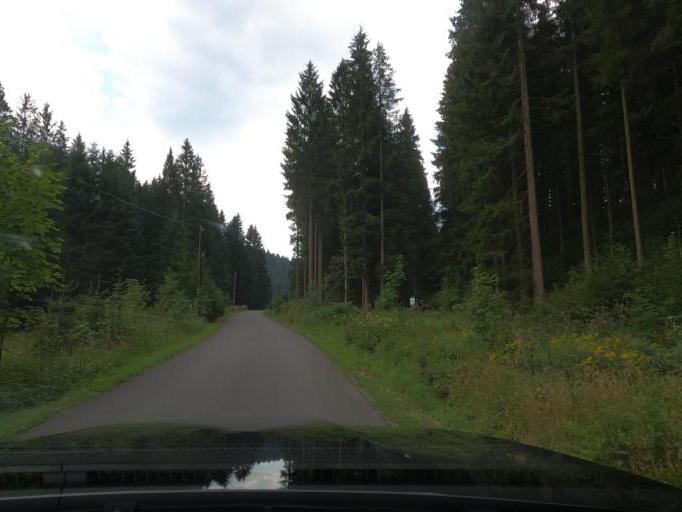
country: DE
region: Lower Saxony
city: Wildemann
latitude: 51.7950
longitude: 10.3007
